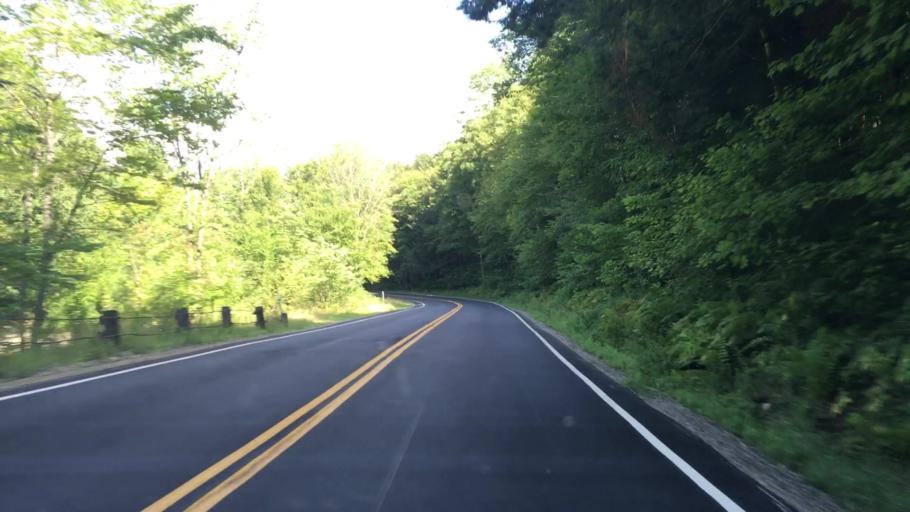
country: US
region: New Hampshire
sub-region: Grafton County
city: North Haverhill
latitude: 44.1067
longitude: -71.8930
